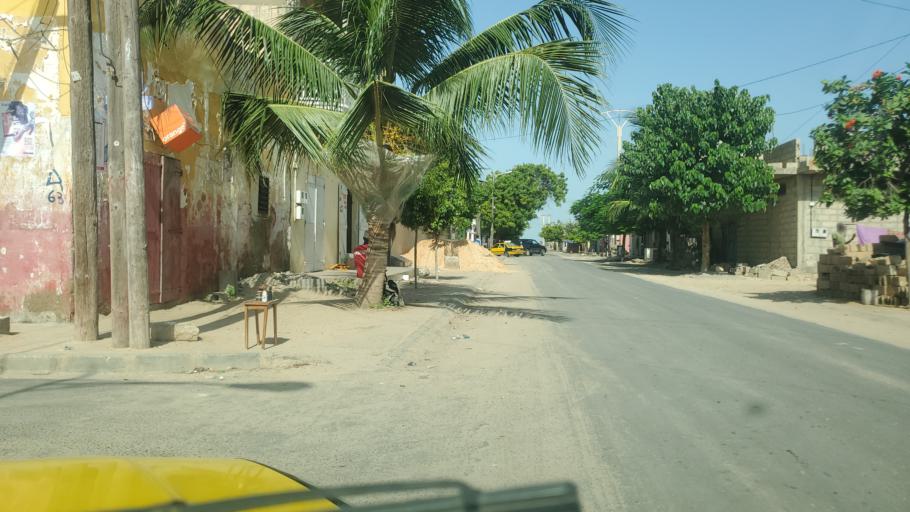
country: SN
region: Saint-Louis
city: Saint-Louis
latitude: 16.0191
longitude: -16.4854
